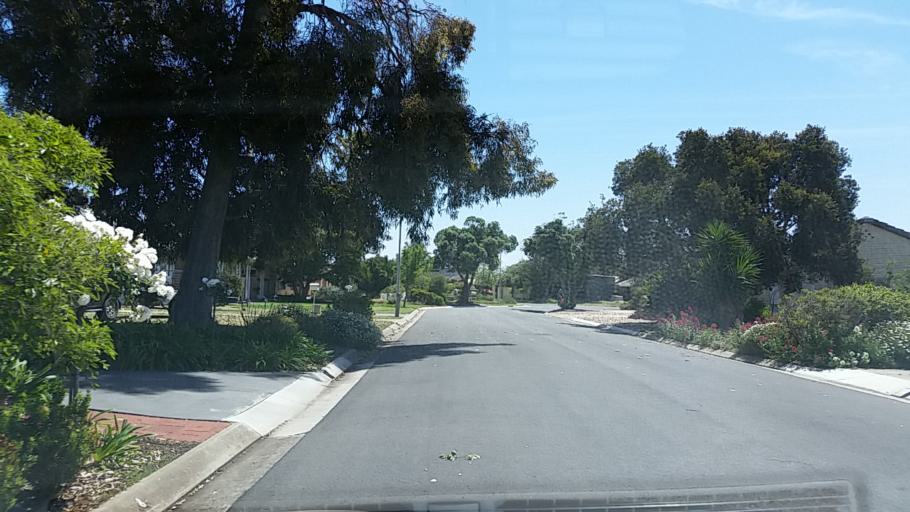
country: AU
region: South Australia
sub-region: Charles Sturt
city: Grange
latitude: -34.8989
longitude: 138.4945
